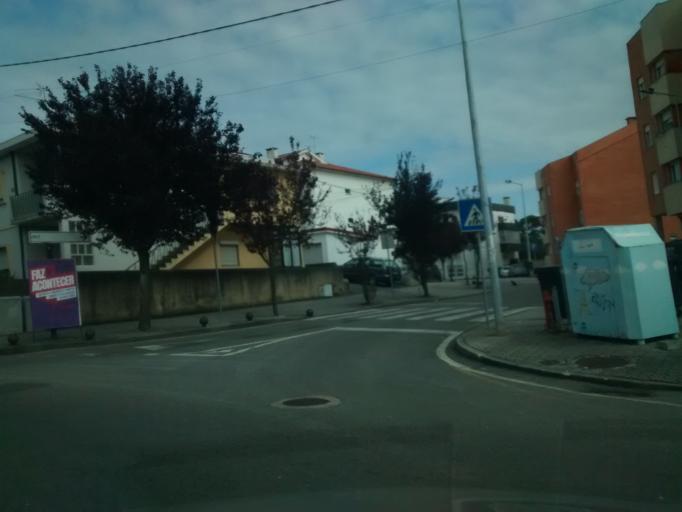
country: PT
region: Aveiro
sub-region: Aveiro
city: Aveiro
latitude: 40.6542
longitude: -8.6235
